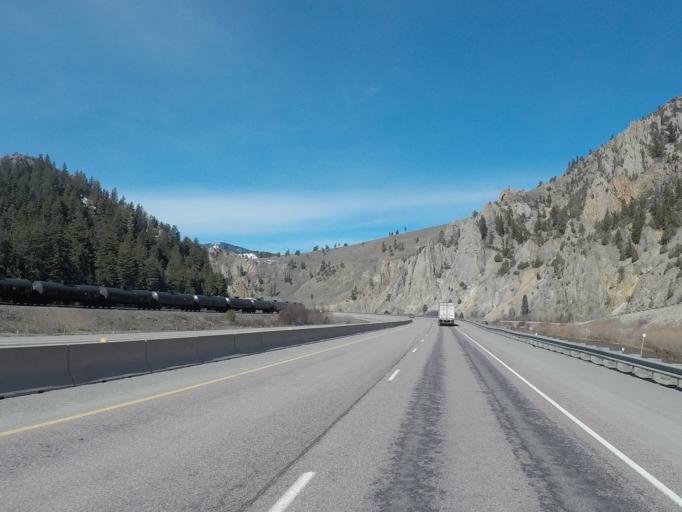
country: US
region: Montana
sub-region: Granite County
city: Philipsburg
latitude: 46.7171
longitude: -113.3101
